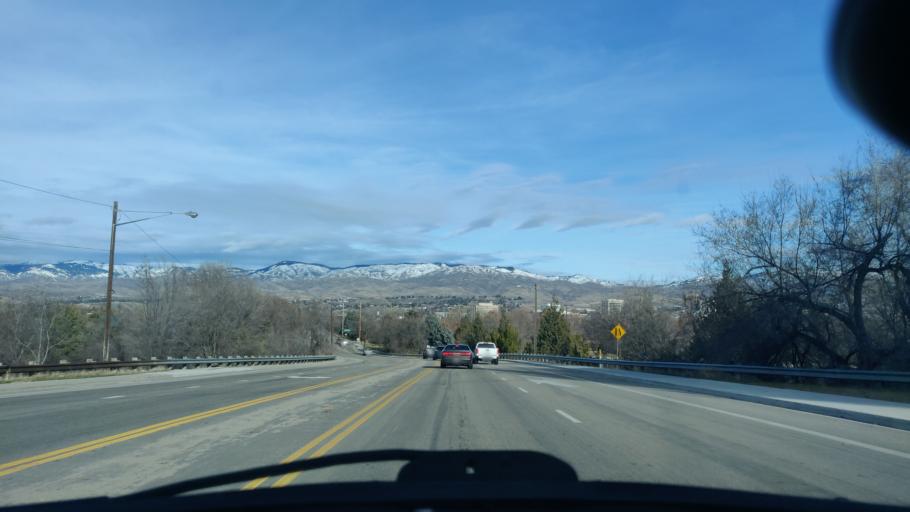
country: US
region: Idaho
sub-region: Ada County
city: Garden City
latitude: 43.6119
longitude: -116.2279
